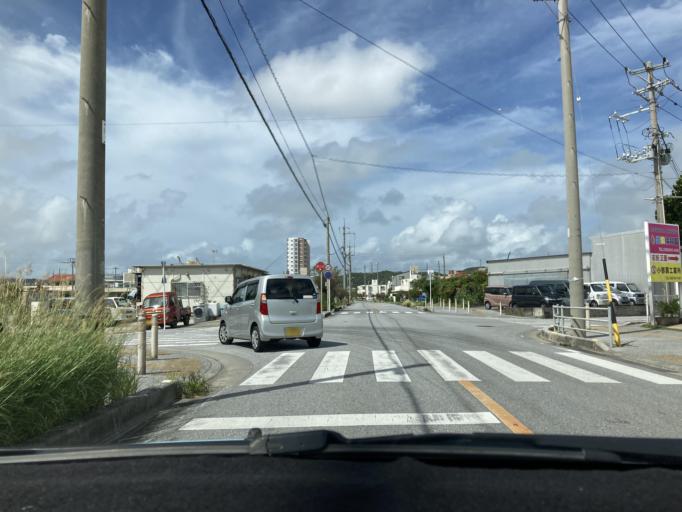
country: JP
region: Okinawa
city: Ginowan
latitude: 26.2232
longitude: 127.7704
